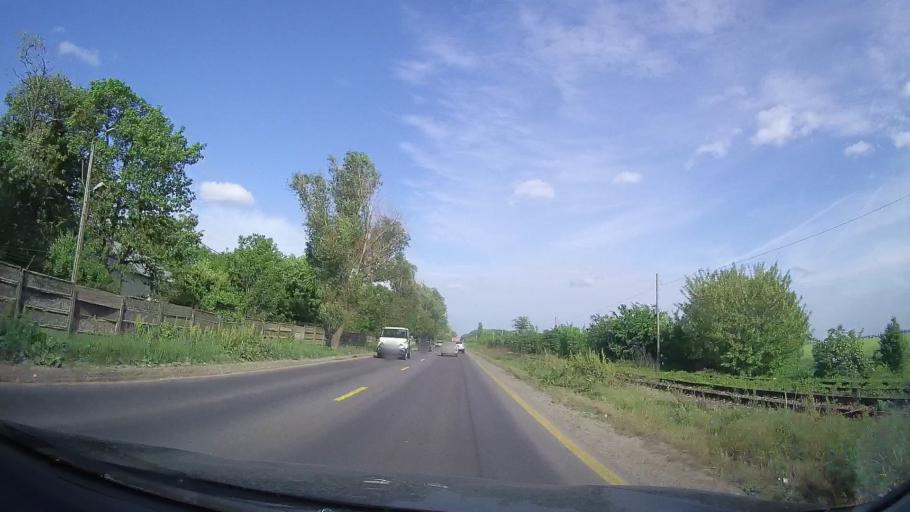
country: RO
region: Ilfov
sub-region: Comuna Magurele
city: Alunisu
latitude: 44.3493
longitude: 26.0672
